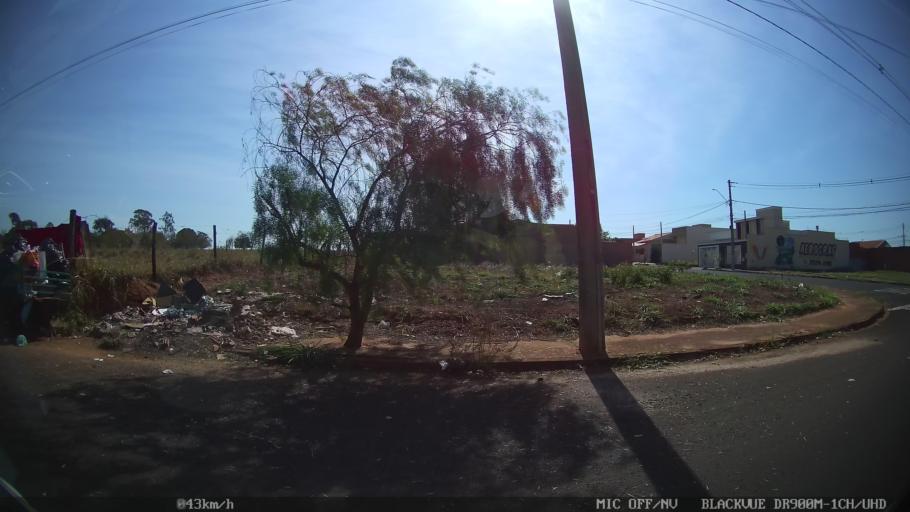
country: BR
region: Sao Paulo
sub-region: Sao Jose Do Rio Preto
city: Sao Jose do Rio Preto
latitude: -20.7931
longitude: -49.4420
